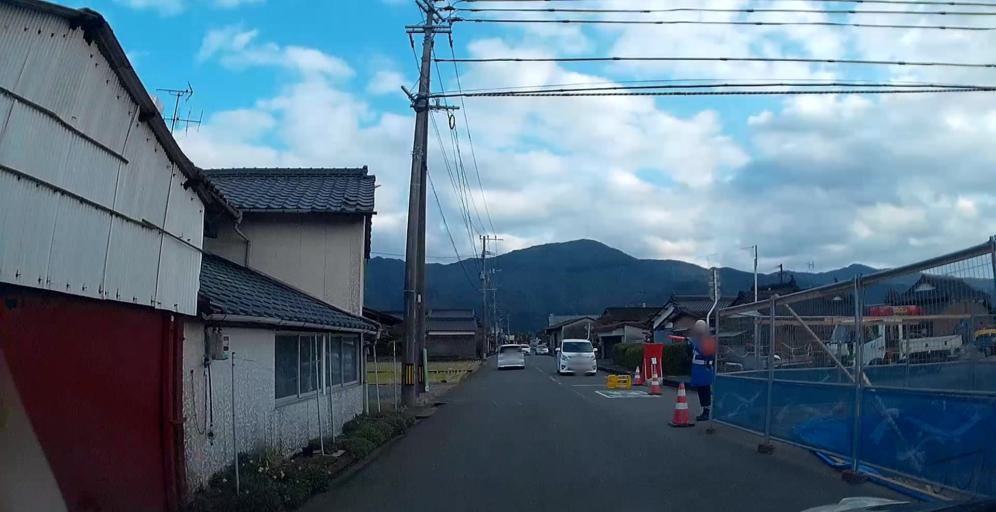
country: JP
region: Kumamoto
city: Yatsushiro
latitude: 32.5356
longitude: 130.6476
